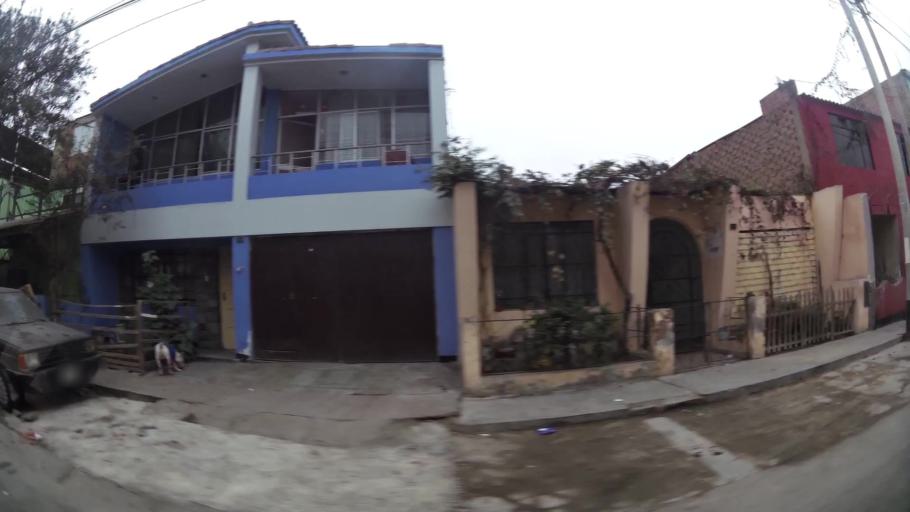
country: PE
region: Lima
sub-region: Lima
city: Surco
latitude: -12.1703
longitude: -76.9761
